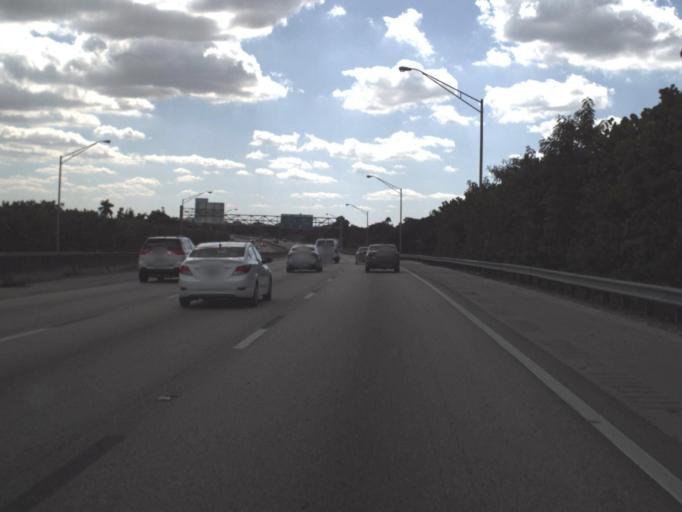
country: US
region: Florida
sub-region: Broward County
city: Pembroke Pines
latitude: 25.9945
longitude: -80.2251
